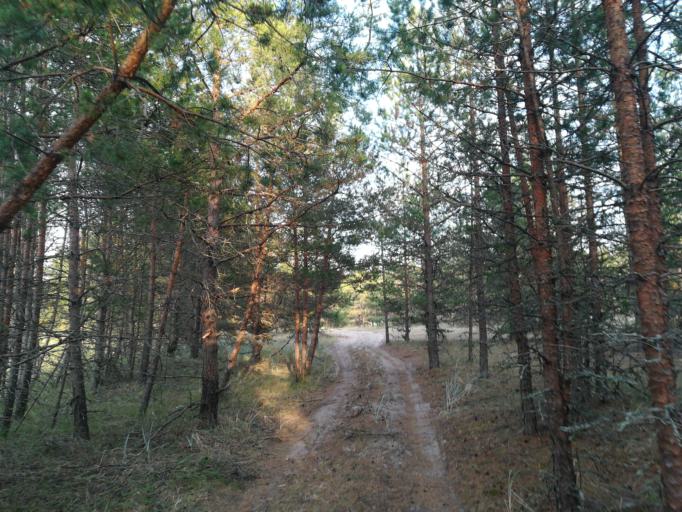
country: RU
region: Leningrad
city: Ust'-Luga
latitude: 59.6771
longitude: 28.2468
